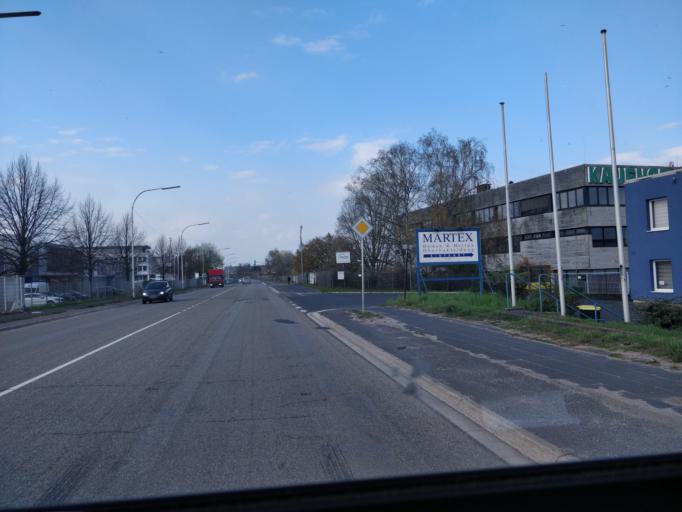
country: DE
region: North Rhine-Westphalia
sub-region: Regierungsbezirk Koln
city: Frechen
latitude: 50.9168
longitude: 6.8267
